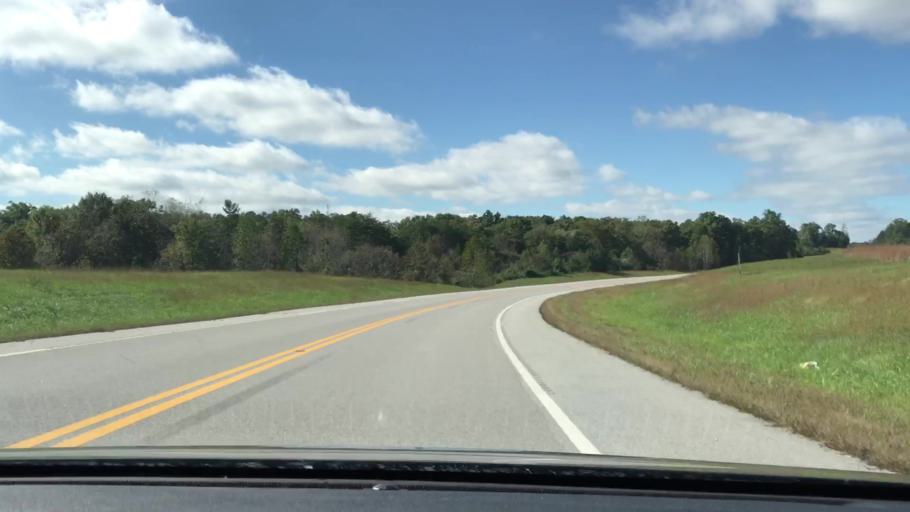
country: US
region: Tennessee
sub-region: Fentress County
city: Jamestown
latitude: 36.3537
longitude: -84.7326
